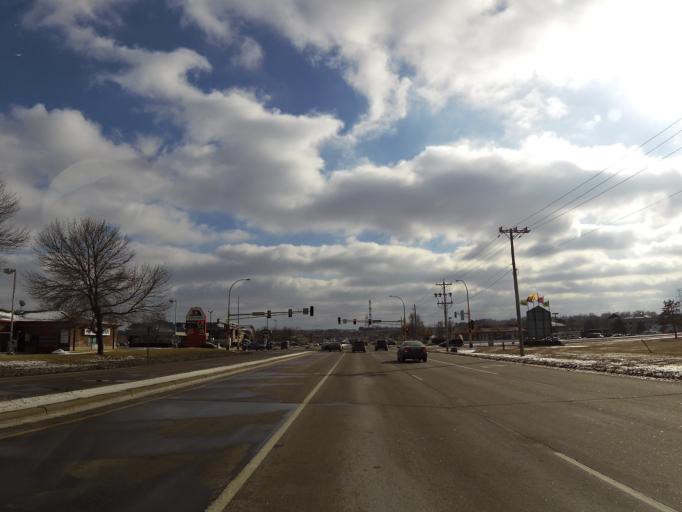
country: US
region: Minnesota
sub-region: Scott County
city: Shakopee
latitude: 44.7859
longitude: -93.4698
